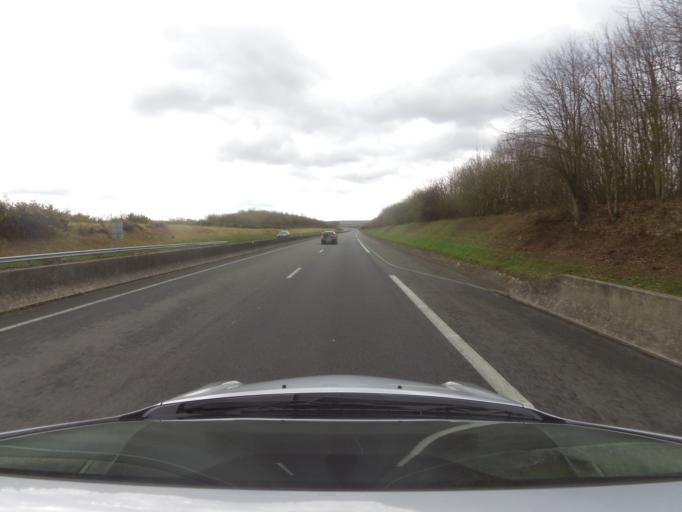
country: FR
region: Nord-Pas-de-Calais
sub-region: Departement du Pas-de-Calais
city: Saint-Josse
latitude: 50.4605
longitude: 1.7013
